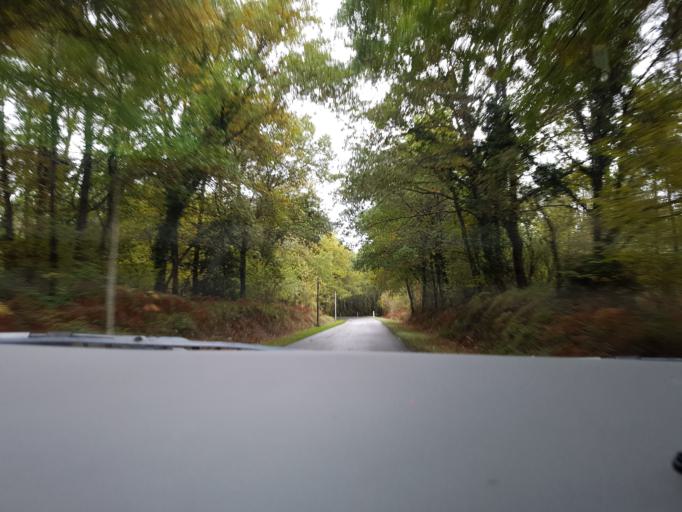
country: FR
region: Aquitaine
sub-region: Departement des Landes
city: Roquefort
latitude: 44.0521
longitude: -0.3427
